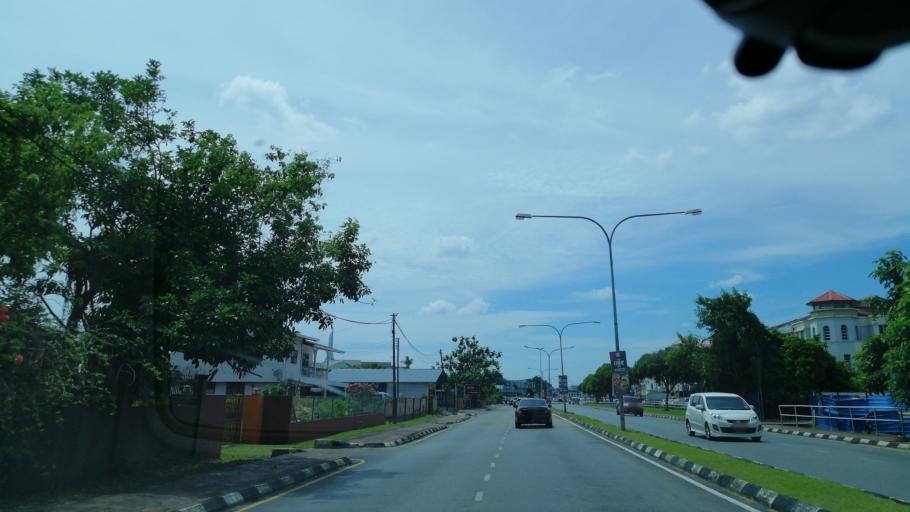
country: MY
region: Sarawak
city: Kuching
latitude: 1.5435
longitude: 110.3578
